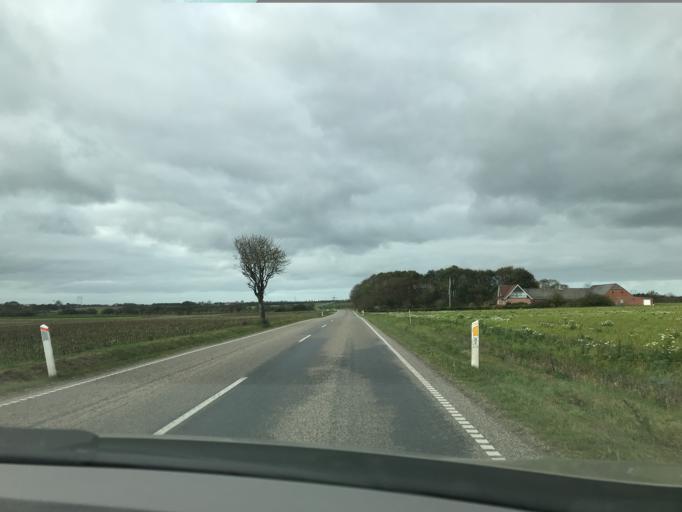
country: DK
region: South Denmark
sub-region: Varde Kommune
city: Olgod
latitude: 55.7897
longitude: 8.6879
